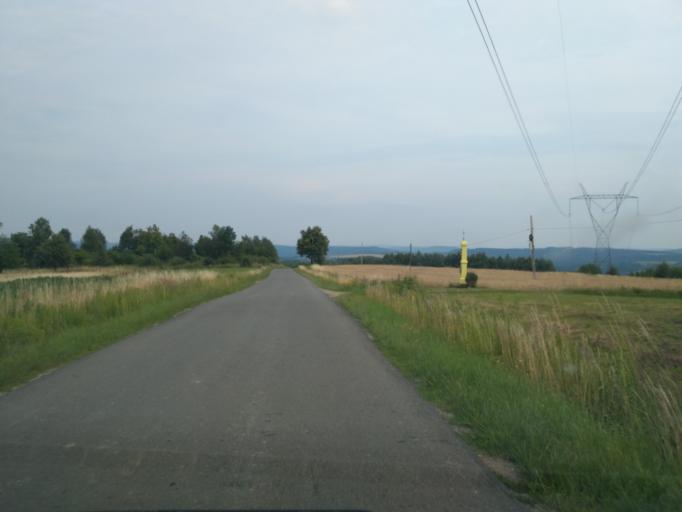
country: PL
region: Subcarpathian Voivodeship
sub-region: Powiat strzyzowski
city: Jawornik
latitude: 49.8677
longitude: 21.8628
